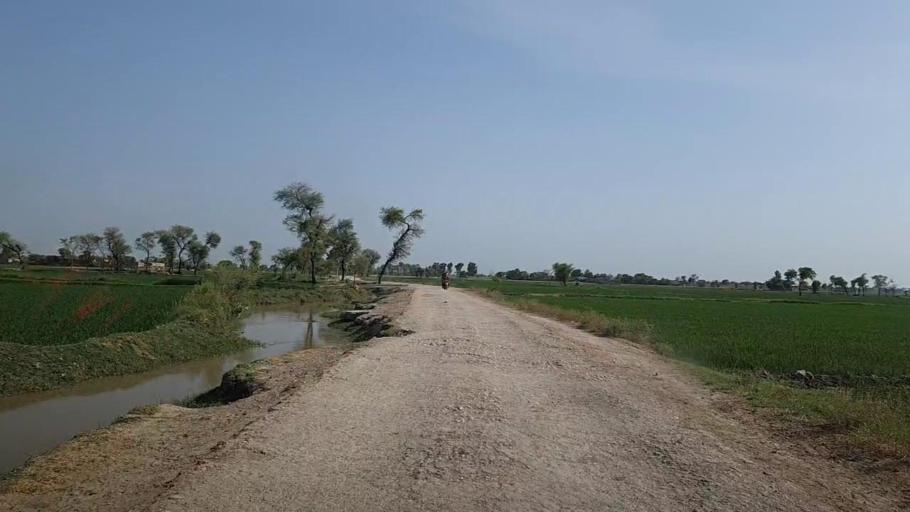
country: PK
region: Sindh
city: Sita Road
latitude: 27.1000
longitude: 67.8524
